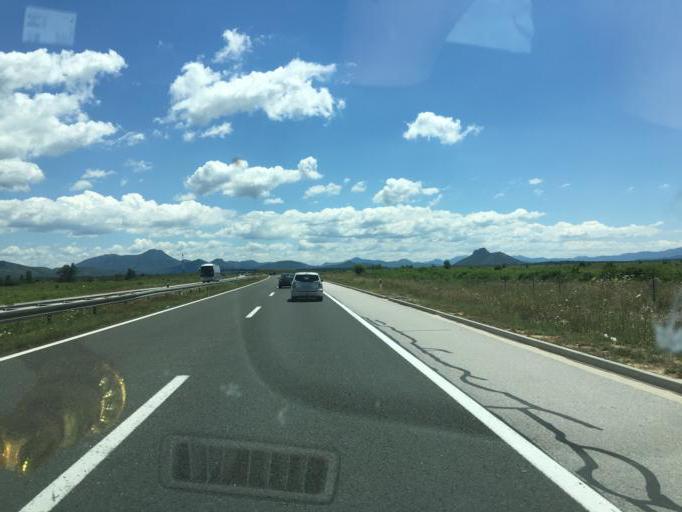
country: HR
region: Licko-Senjska
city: Gospic
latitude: 44.4834
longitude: 15.5529
